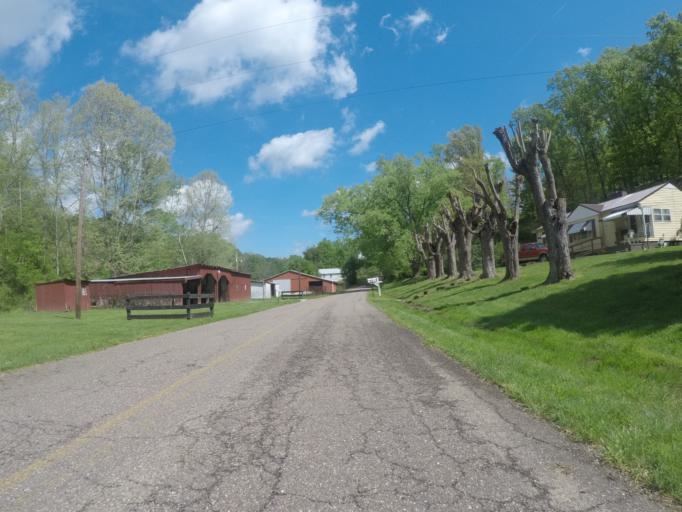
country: US
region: West Virginia
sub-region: Cabell County
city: Huntington
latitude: 38.5250
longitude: -82.4407
